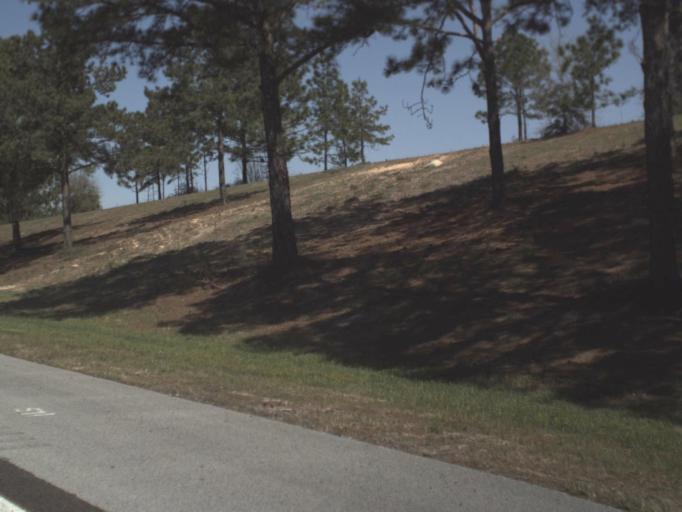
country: US
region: Florida
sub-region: Walton County
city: DeFuniak Springs
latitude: 30.7279
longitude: -86.2123
